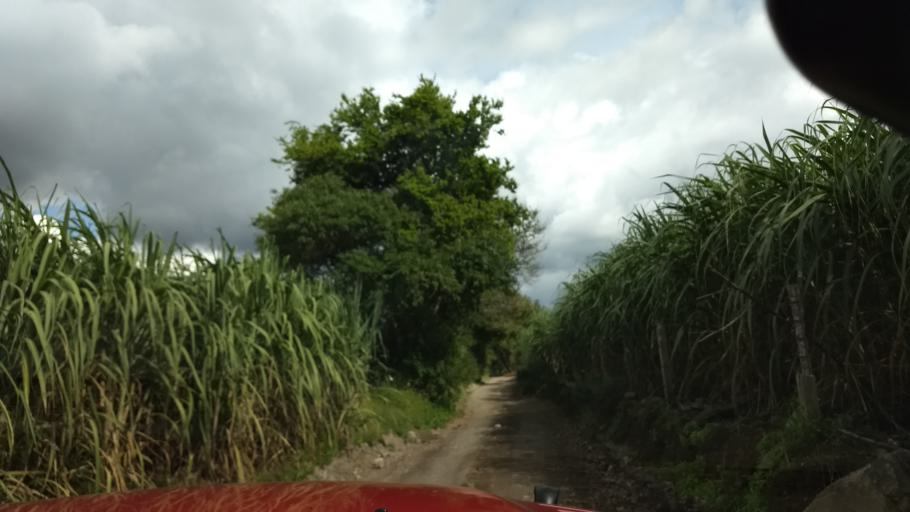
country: MX
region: Colima
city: Suchitlan
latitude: 19.4613
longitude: -103.7598
